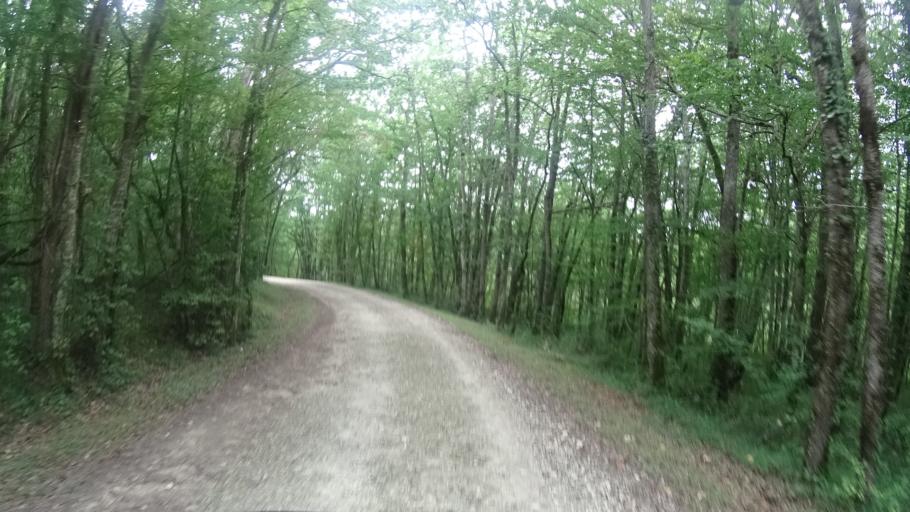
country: FR
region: Aquitaine
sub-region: Departement de la Dordogne
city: Lembras
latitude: 45.0019
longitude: 0.5451
